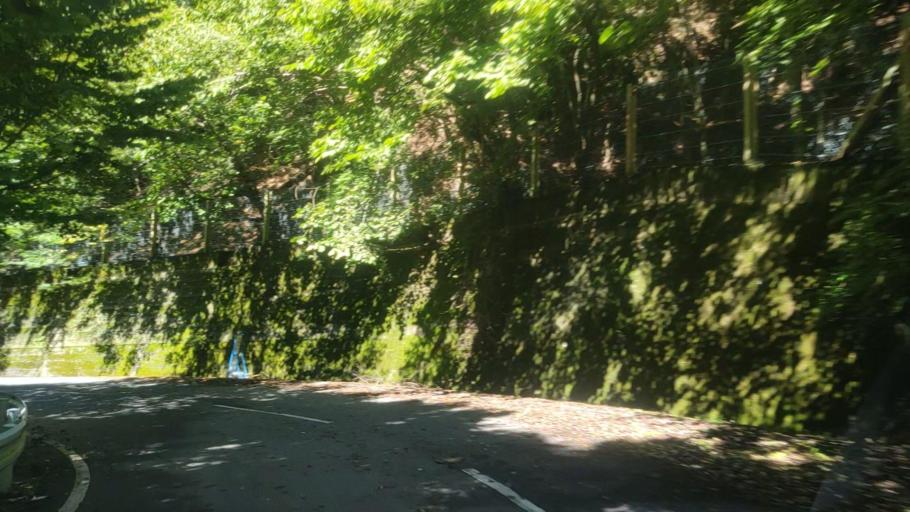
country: JP
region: Yamanashi
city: Fujikawaguchiko
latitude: 35.5677
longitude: 138.7867
